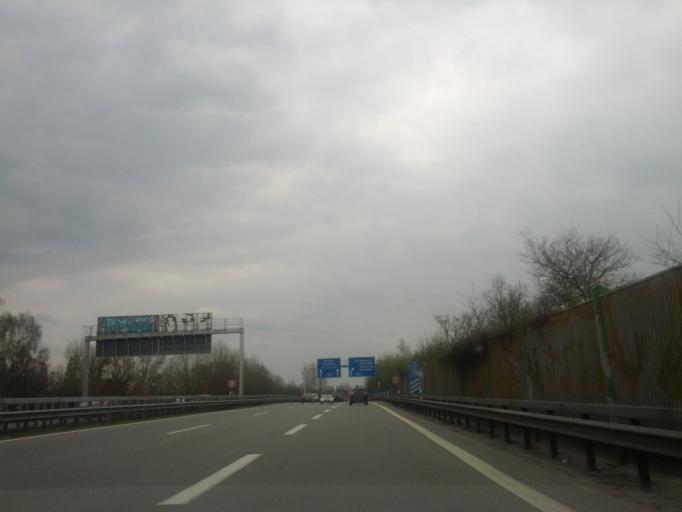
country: DE
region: Lower Saxony
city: Oldenburg
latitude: 53.1502
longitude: 8.1933
